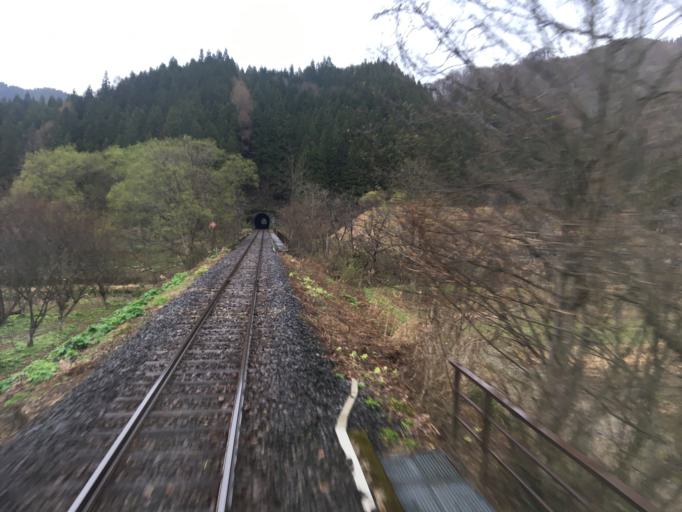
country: JP
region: Akita
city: Kakunodatemachi
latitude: 39.7020
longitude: 140.5550
